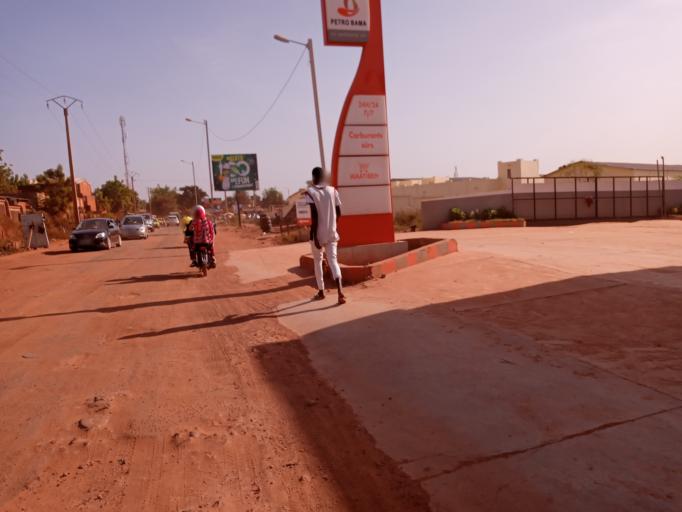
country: ML
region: Bamako
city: Bamako
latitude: 12.6237
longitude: -7.9549
